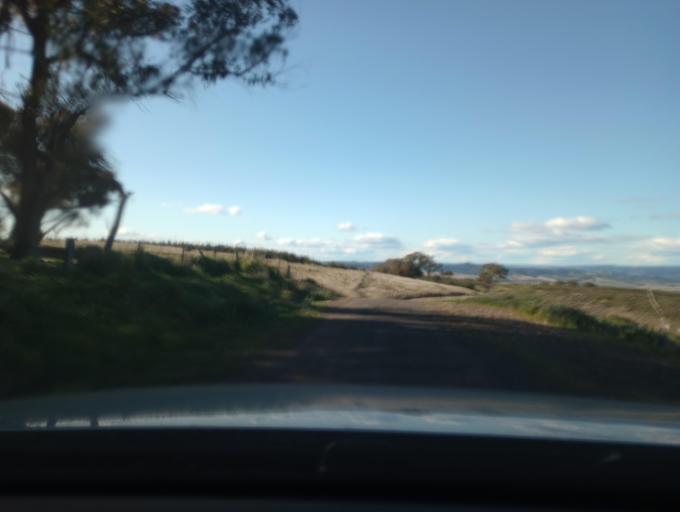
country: AU
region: New South Wales
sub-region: Blayney
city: Blayney
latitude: -33.4187
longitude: 149.3137
